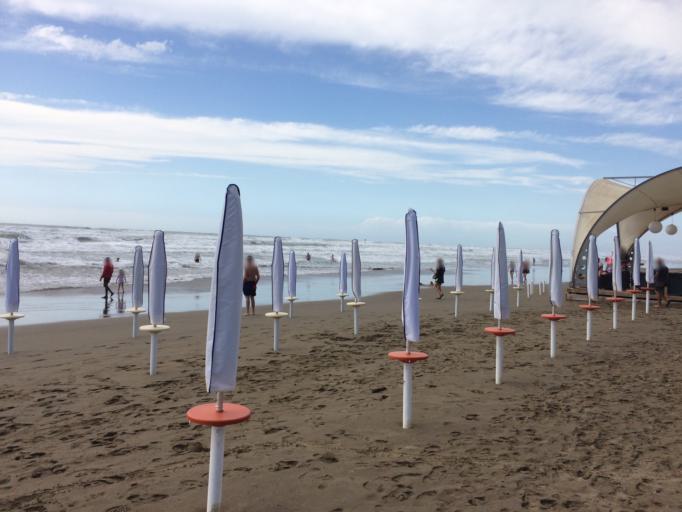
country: IT
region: Tuscany
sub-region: Provincia di Livorno
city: Donoratico
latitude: 43.1523
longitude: 10.5399
